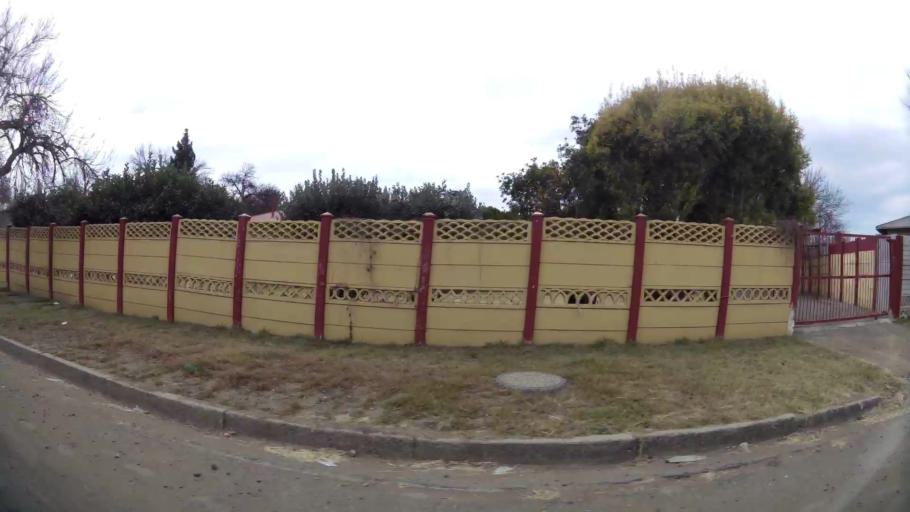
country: ZA
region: Orange Free State
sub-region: Fezile Dabi District Municipality
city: Kroonstad
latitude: -27.6763
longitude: 27.2321
